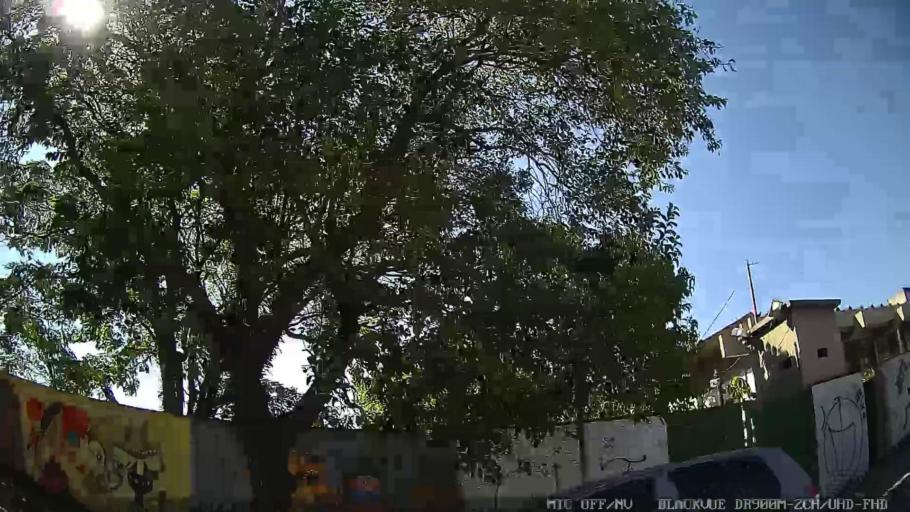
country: BR
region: Sao Paulo
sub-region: Sao Caetano Do Sul
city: Sao Caetano do Sul
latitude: -23.5499
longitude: -46.4866
